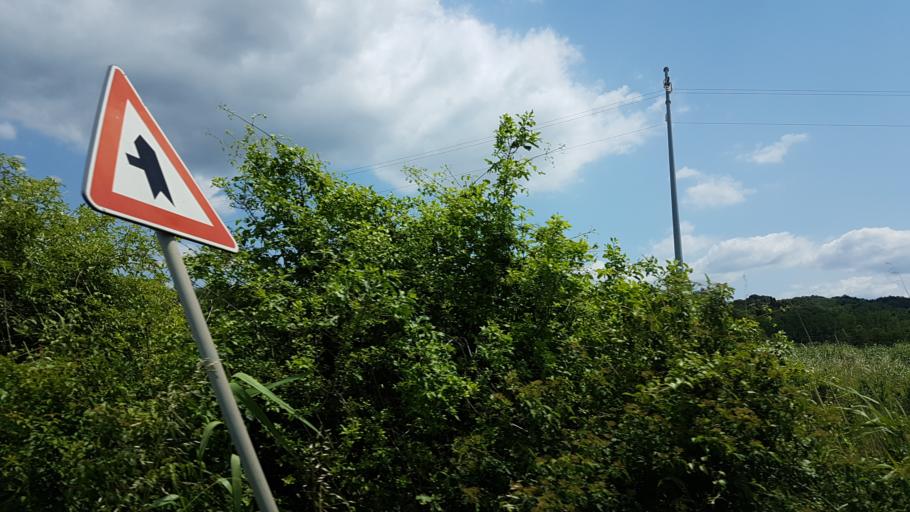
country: IT
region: Tuscany
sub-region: Provincia di Livorno
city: Collesalvetti
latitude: 43.5639
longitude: 10.4766
